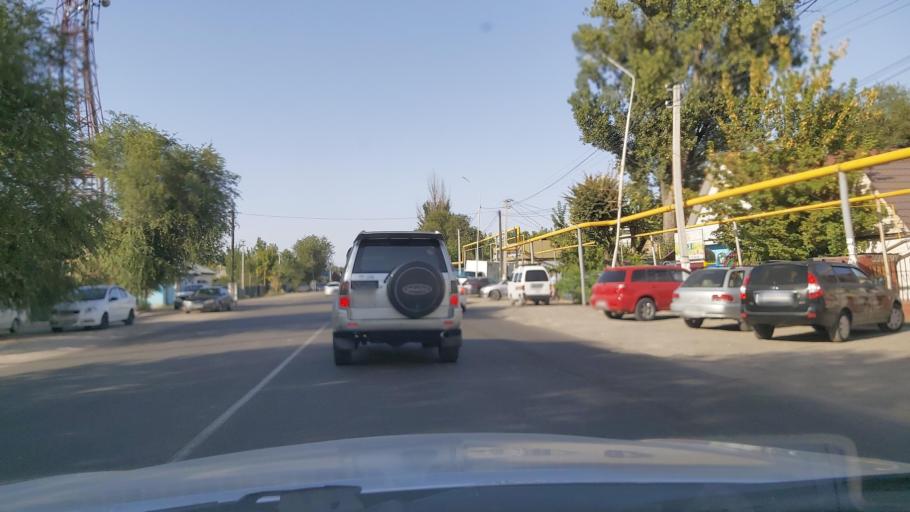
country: KZ
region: Almaty Oblysy
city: Energeticheskiy
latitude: 43.4809
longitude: 77.0331
